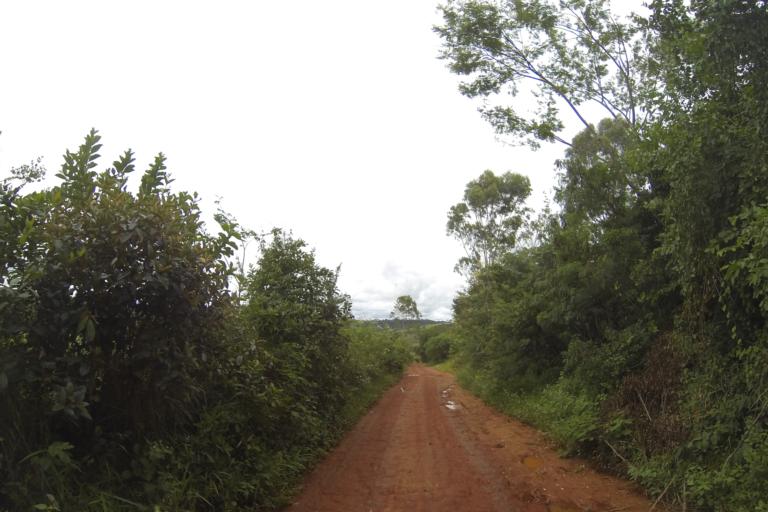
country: BR
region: Minas Gerais
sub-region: Ibia
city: Ibia
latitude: -19.6788
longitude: -46.6801
